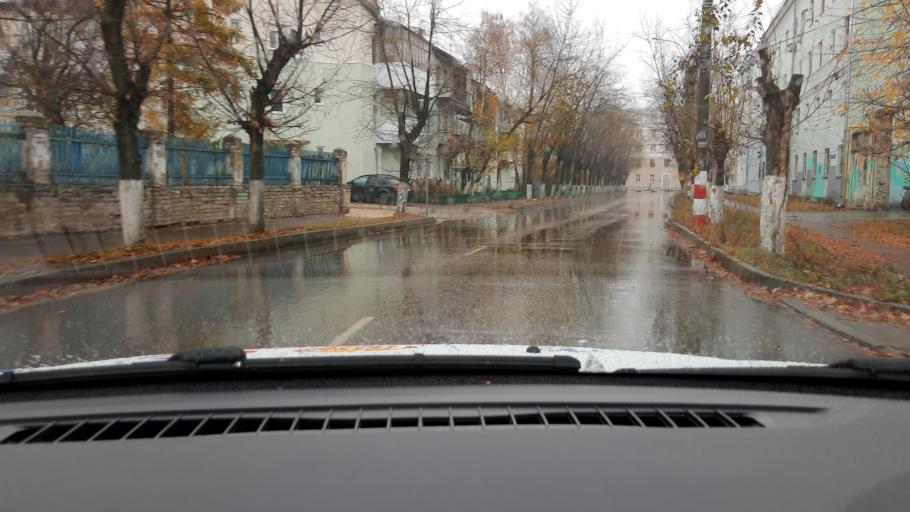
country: RU
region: Nizjnij Novgorod
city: Dzerzhinsk
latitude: 56.2409
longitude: 43.4634
